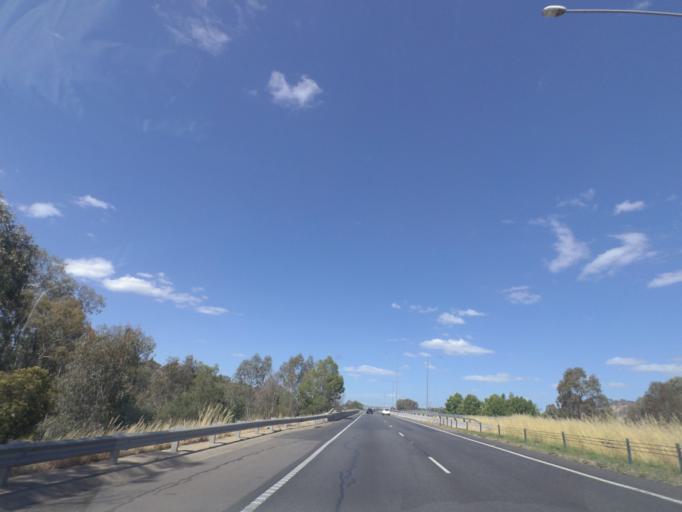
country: AU
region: Victoria
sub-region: Wodonga
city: Wodonga
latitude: -36.1107
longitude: 146.8924
